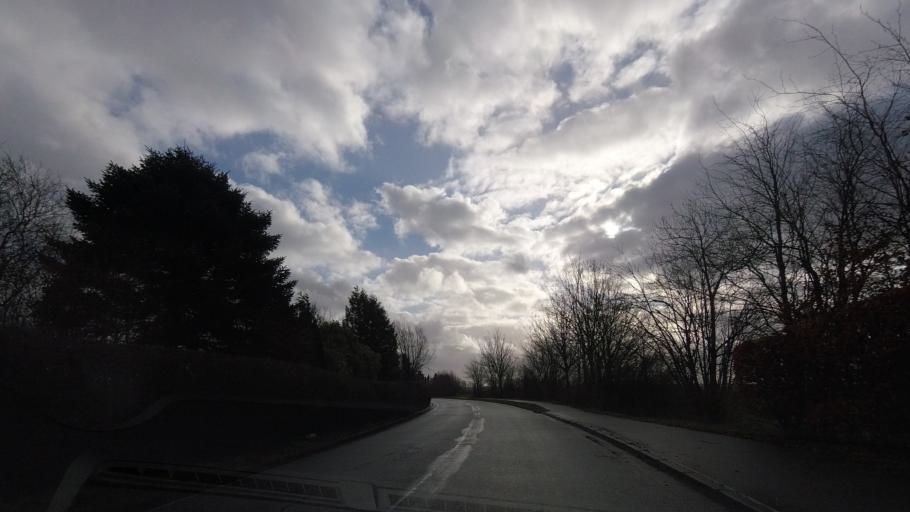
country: DE
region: Schleswig-Holstein
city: Grodersby
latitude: 54.6362
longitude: 9.9205
